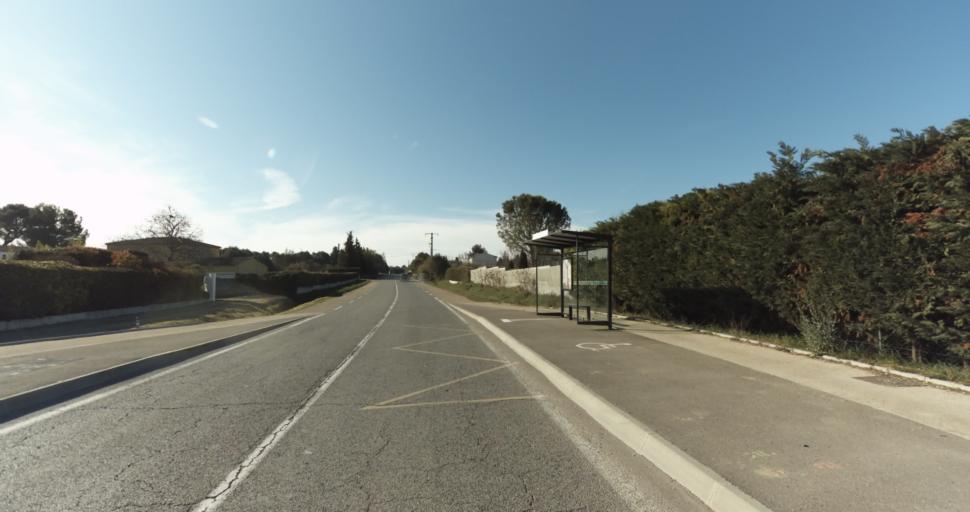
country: FR
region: Provence-Alpes-Cote d'Azur
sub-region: Departement des Bouches-du-Rhone
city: Aix-en-Provence
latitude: 43.5697
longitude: 5.4331
